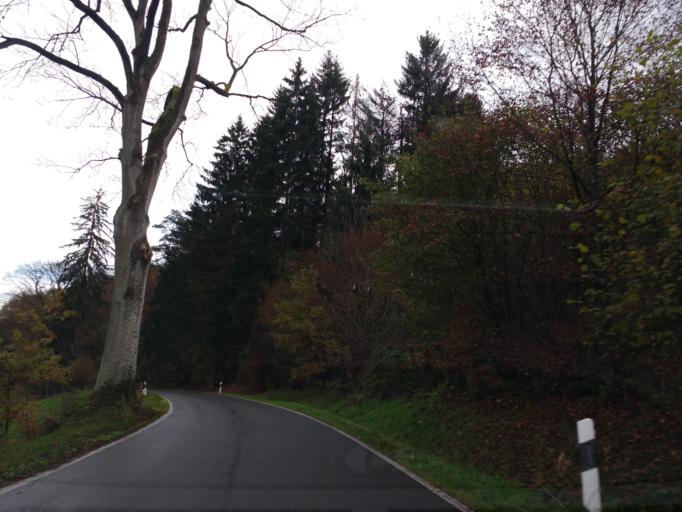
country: DE
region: Hesse
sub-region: Regierungsbezirk Kassel
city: Vohl
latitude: 51.1968
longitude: 8.9404
